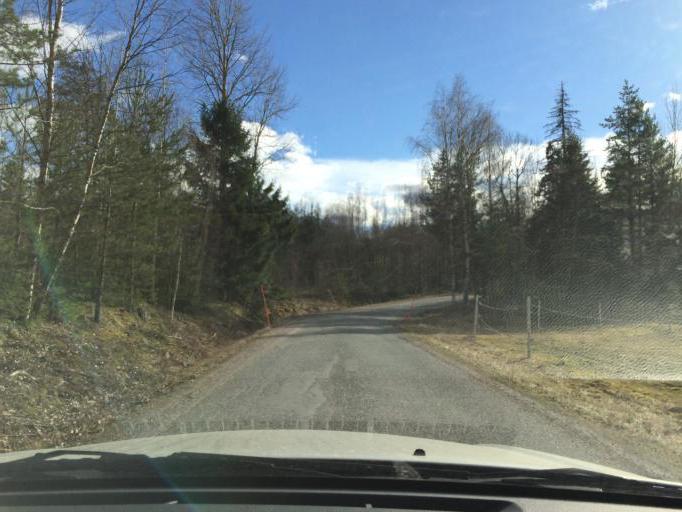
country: SE
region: Soedermanland
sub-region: Eskilstuna Kommun
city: Hallbybrunn
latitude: 59.4276
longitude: 16.4162
